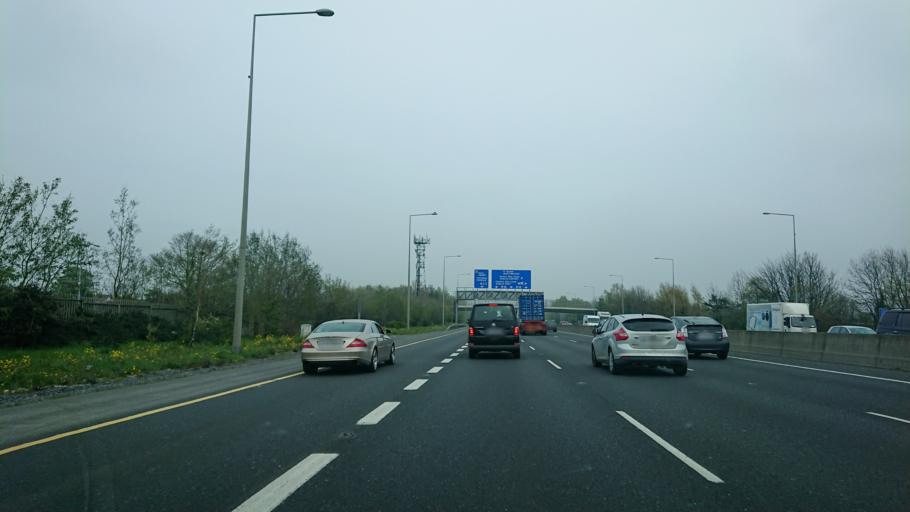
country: IE
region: Leinster
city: Castleknock
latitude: 53.3957
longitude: -6.3423
